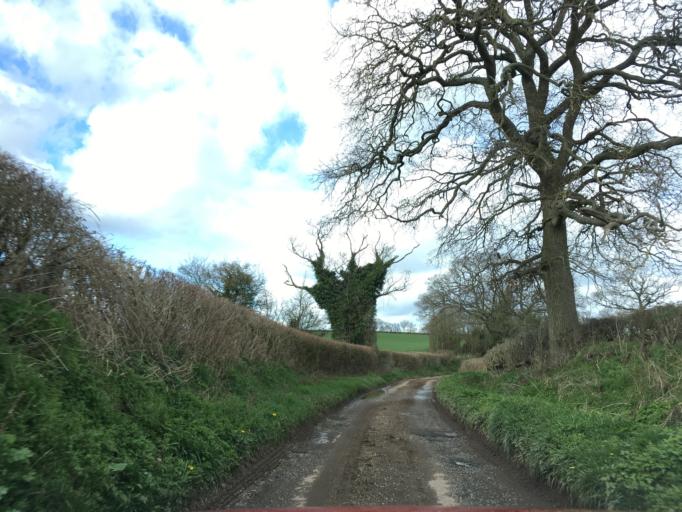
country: GB
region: England
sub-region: Gloucestershire
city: Newent
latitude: 51.8509
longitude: -2.3854
